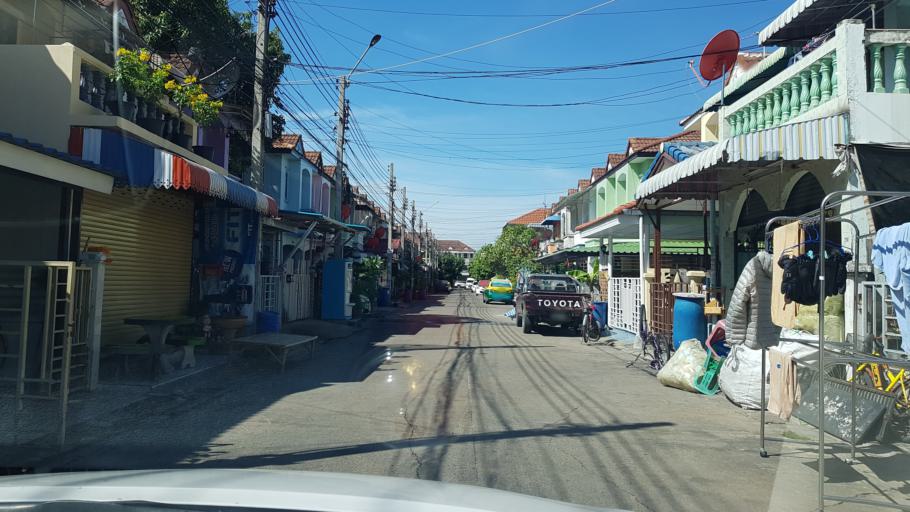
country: TH
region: Bangkok
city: Khlong Sam Wa
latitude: 13.8848
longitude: 100.7164
